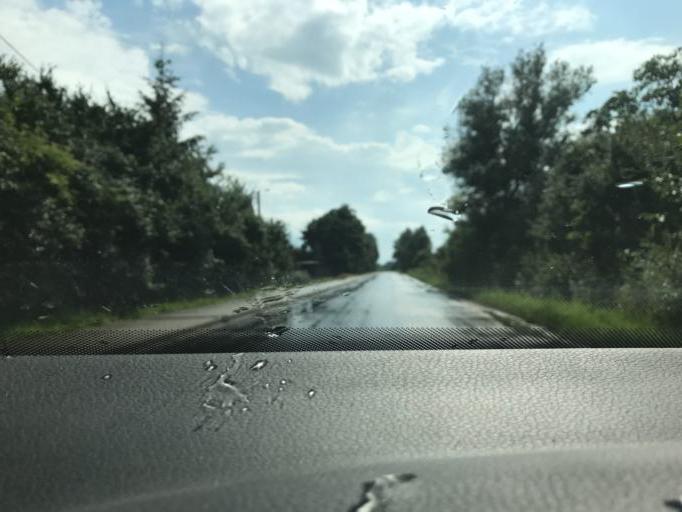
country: PL
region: Pomeranian Voivodeship
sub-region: Powiat gdanski
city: Cedry Wielkie
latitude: 54.3343
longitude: 18.7957
